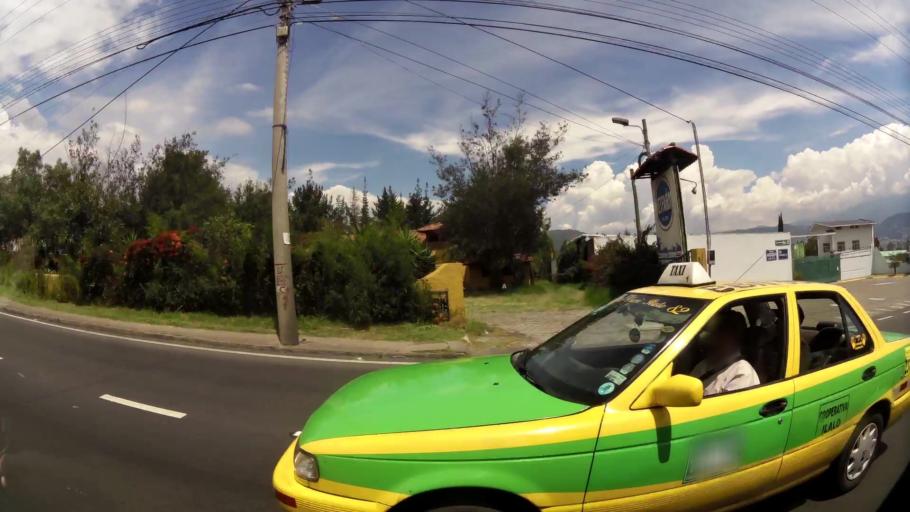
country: EC
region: Pichincha
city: Sangolqui
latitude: -0.2138
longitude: -78.3606
